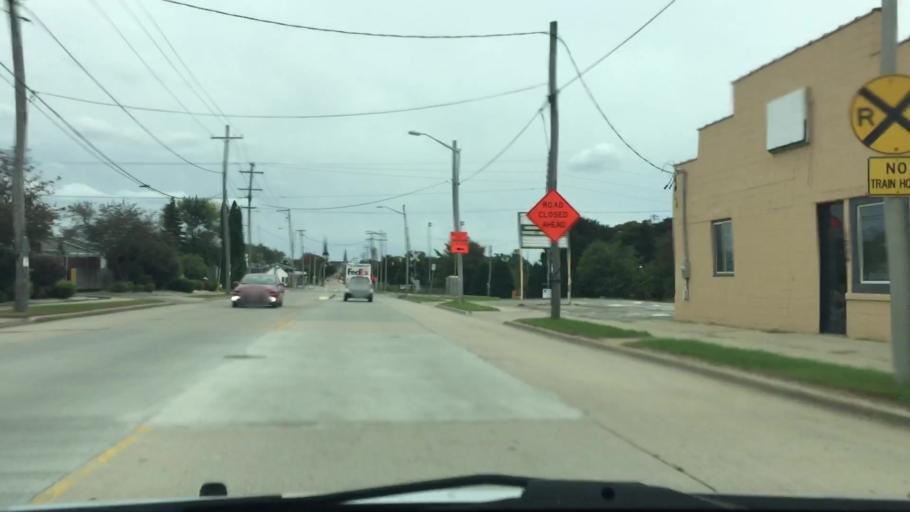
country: US
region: Wisconsin
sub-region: Waukesha County
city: Waukesha
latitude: 43.0203
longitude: -88.2199
